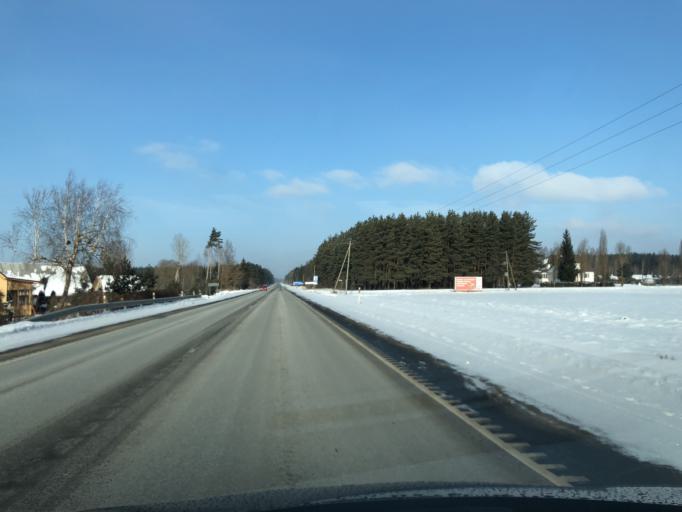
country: EE
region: Tartu
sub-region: Tartu linn
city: Tartu
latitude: 58.3831
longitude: 26.6724
